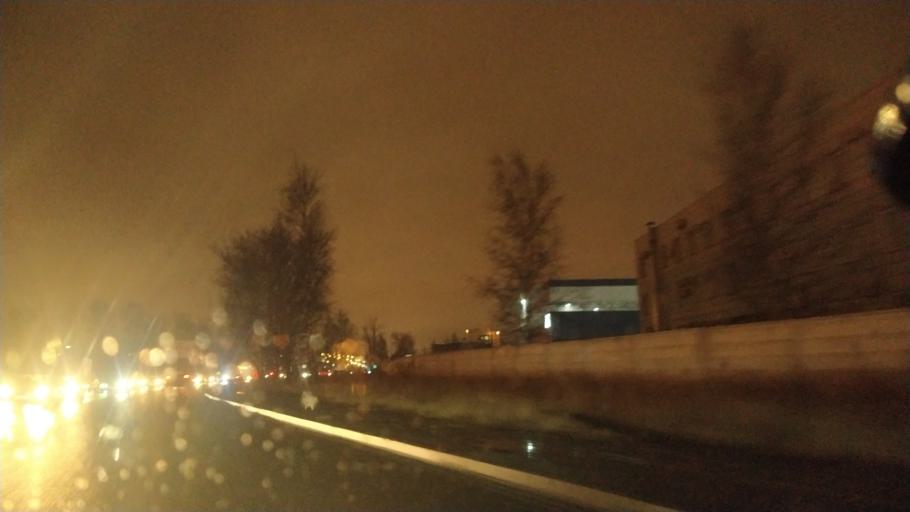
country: RU
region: Leningrad
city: Bugry
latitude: 60.0605
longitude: 30.3854
